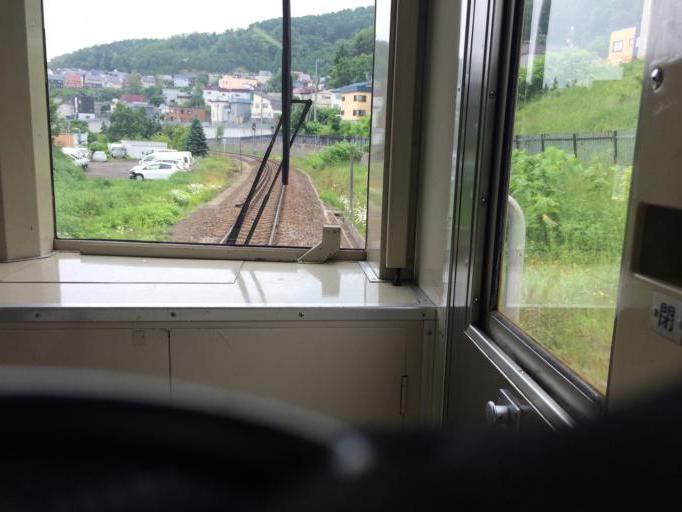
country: JP
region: Hokkaido
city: Otaru
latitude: 43.2037
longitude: 140.9843
